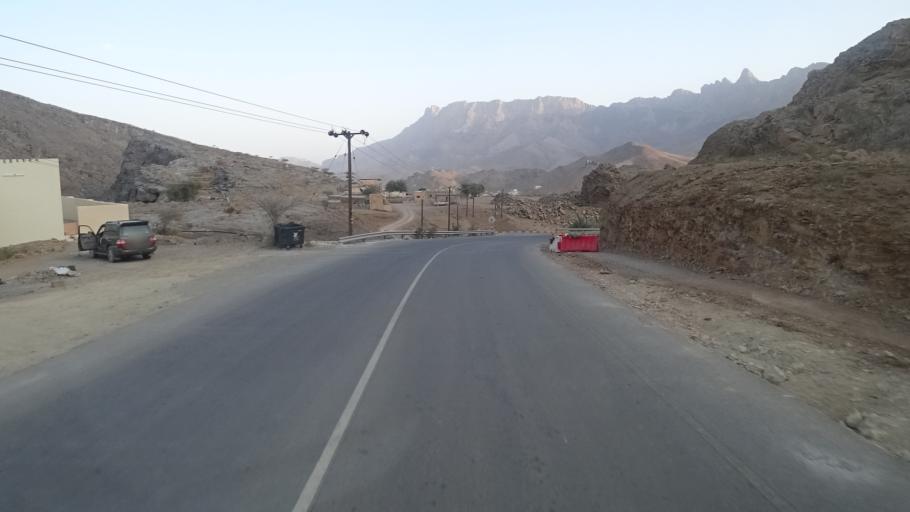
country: OM
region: Muhafazat ad Dakhiliyah
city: Bahla'
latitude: 23.1847
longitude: 57.1411
